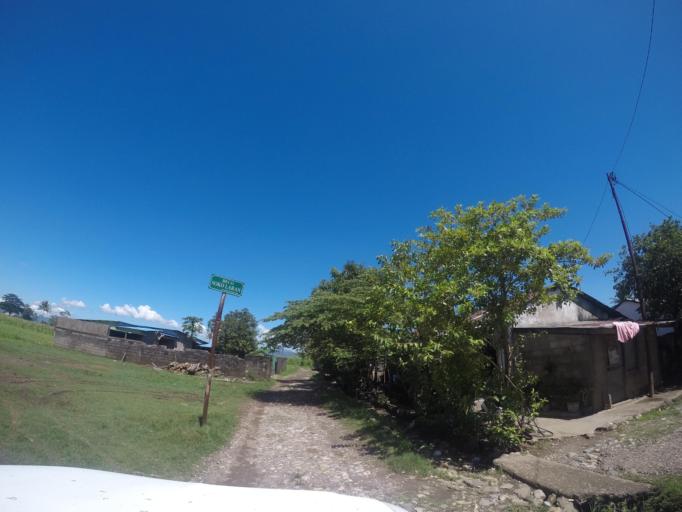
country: TL
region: Bobonaro
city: Maliana
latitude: -8.9832
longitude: 125.2087
